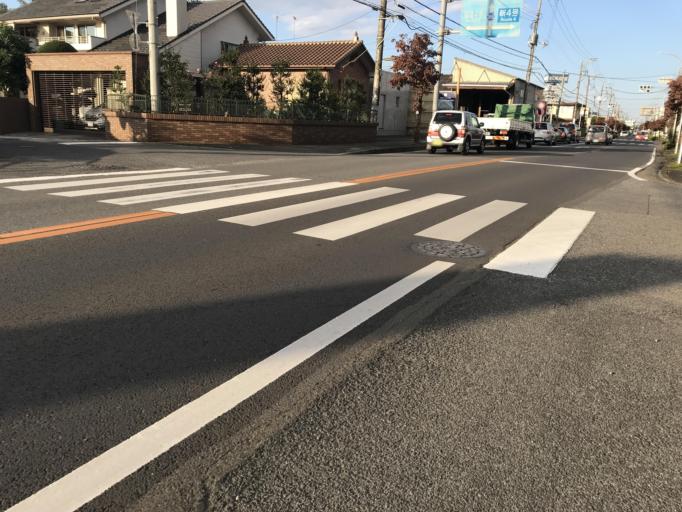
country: JP
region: Tochigi
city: Oyama
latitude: 36.2934
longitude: 139.7893
